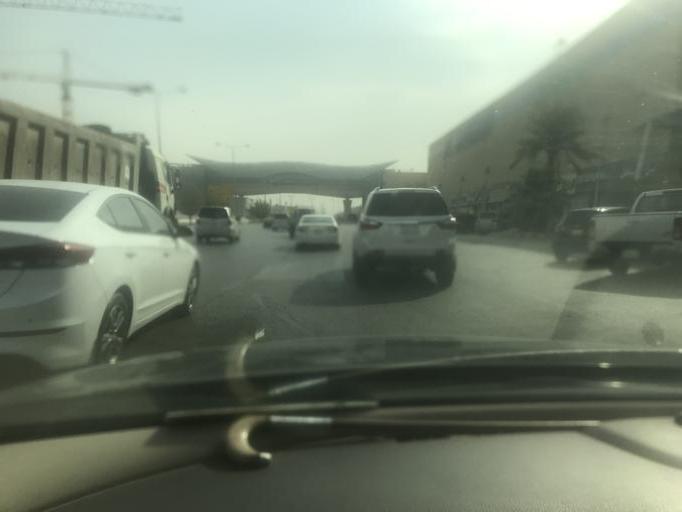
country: SA
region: Ar Riyad
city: Riyadh
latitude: 24.8103
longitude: 46.6237
